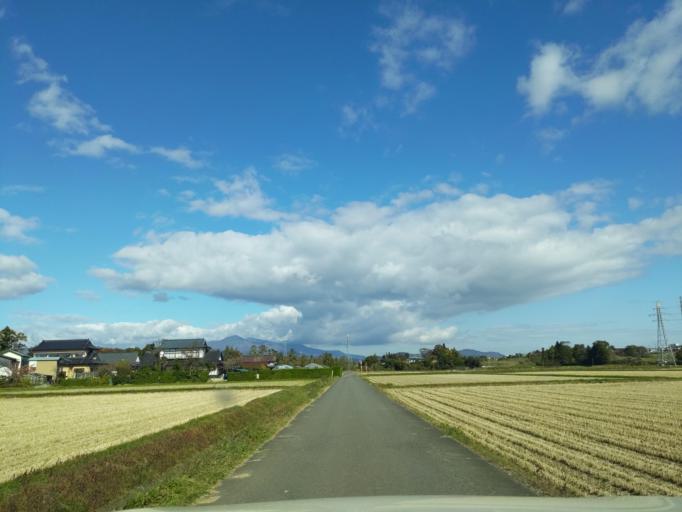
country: JP
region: Fukushima
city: Koriyama
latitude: 37.4251
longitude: 140.3288
